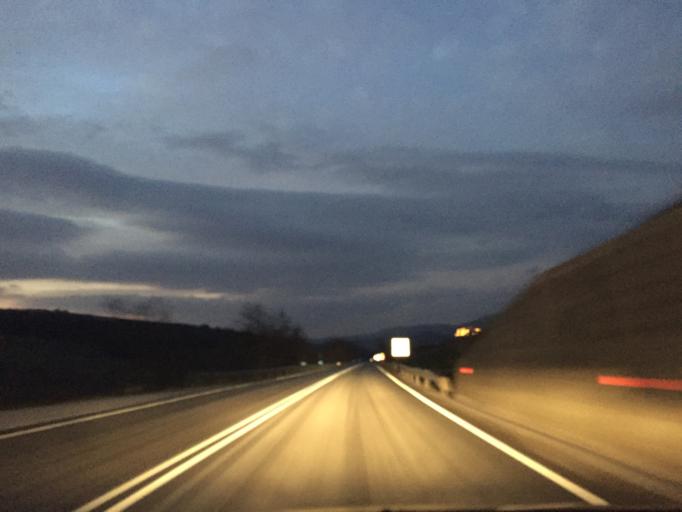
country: IT
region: Apulia
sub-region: Provincia di Foggia
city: Volturara Appula
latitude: 41.4615
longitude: 15.0591
